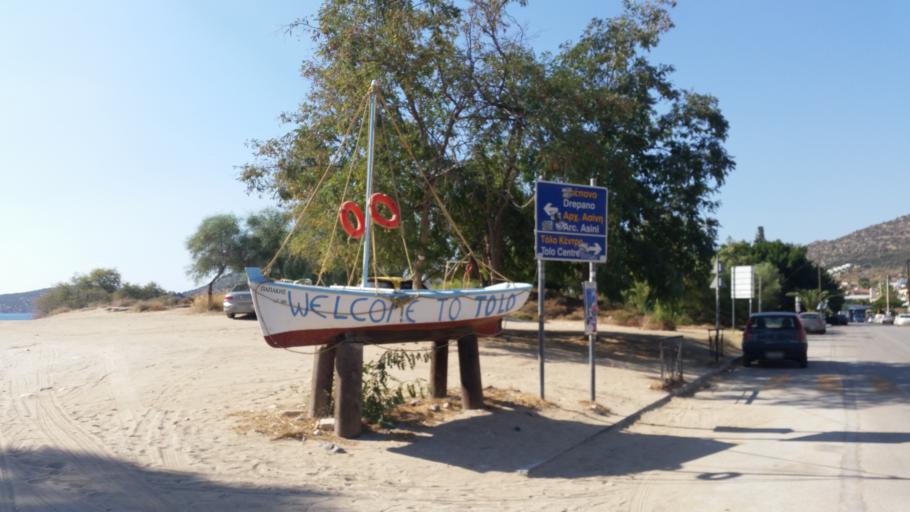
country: GR
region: Peloponnese
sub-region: Nomos Argolidos
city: Tolon
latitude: 37.5269
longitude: 22.8655
